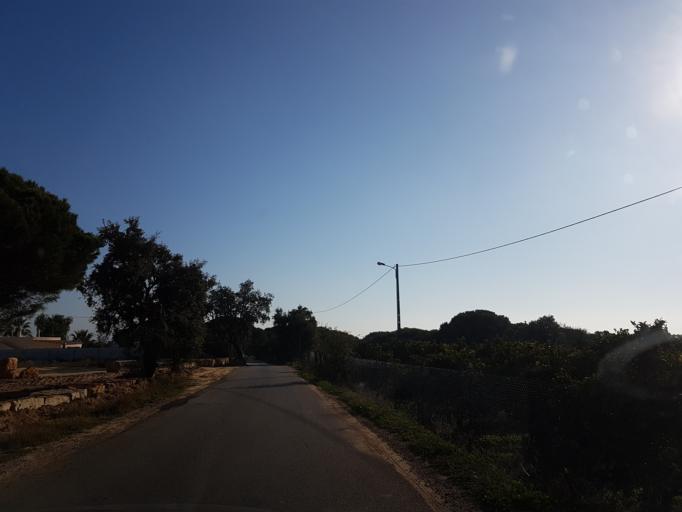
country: PT
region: Faro
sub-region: Albufeira
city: Ferreiras
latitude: 37.0988
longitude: -8.2050
